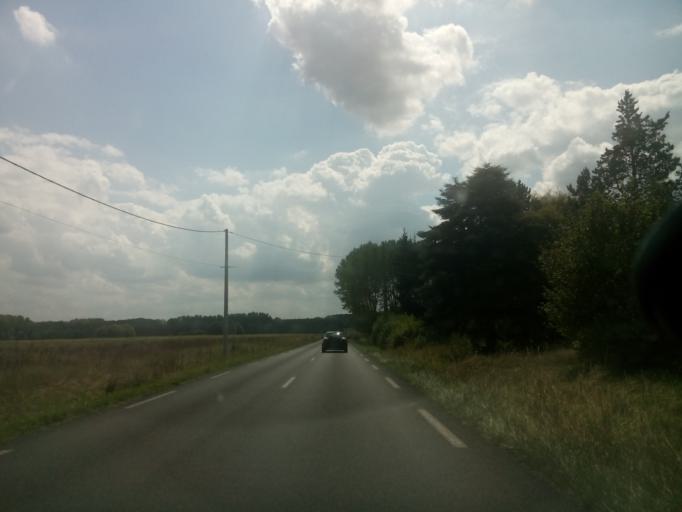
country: FR
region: Centre
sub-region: Departement d'Indre-et-Loire
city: Langeais
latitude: 47.3090
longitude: 0.4108
